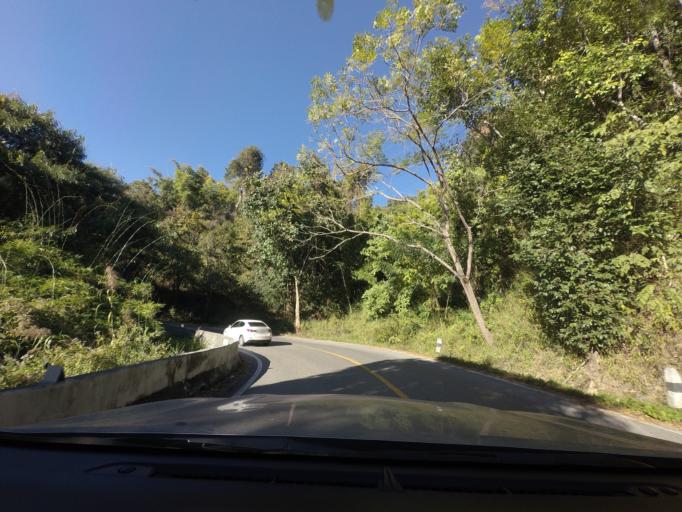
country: TH
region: Mae Hong Son
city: Mae Hi
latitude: 19.2258
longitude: 98.6729
